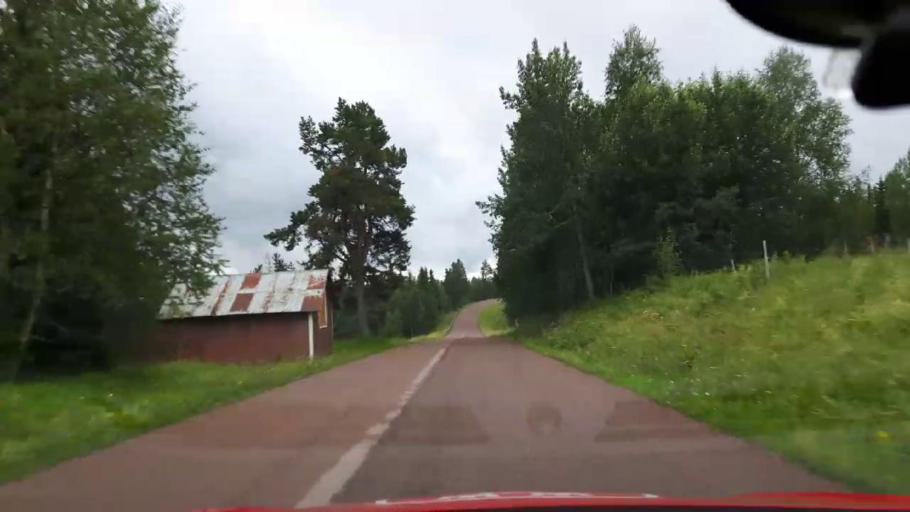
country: SE
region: Jaemtland
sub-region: Krokoms Kommun
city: Valla
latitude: 63.3475
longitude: 13.7223
